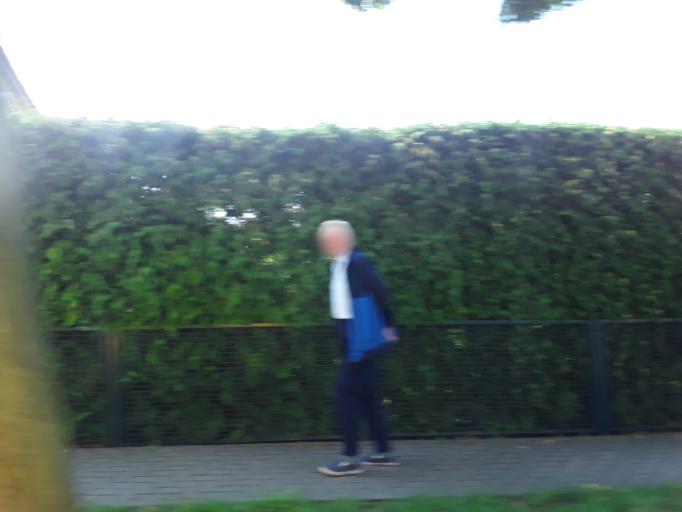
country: DE
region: Berlin
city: Buch
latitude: 52.6282
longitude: 13.5180
